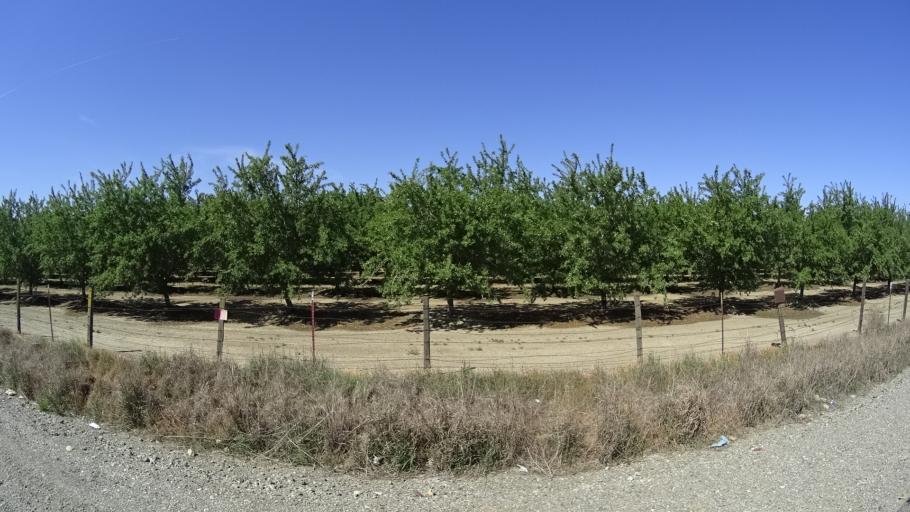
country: US
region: California
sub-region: Glenn County
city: Orland
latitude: 39.7371
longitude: -122.1410
